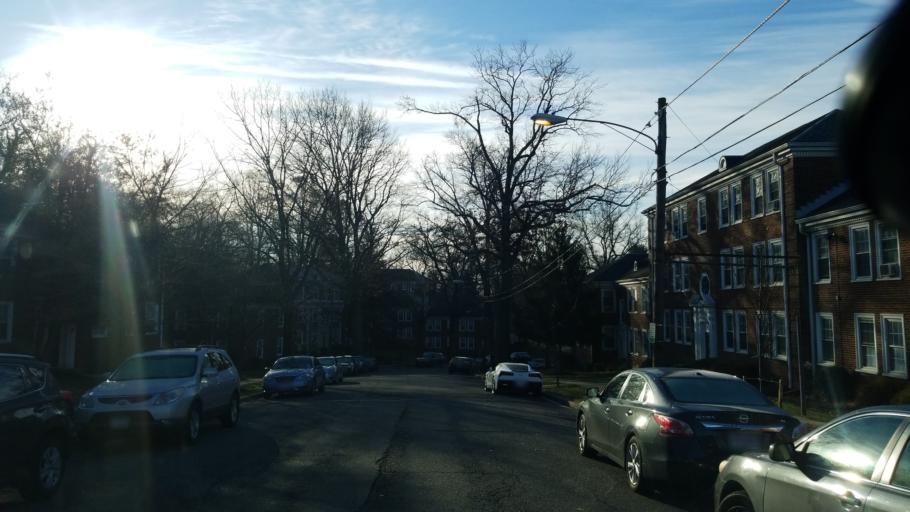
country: US
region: Maryland
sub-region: Prince George's County
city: Silver Hill
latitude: 38.8551
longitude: -76.9638
